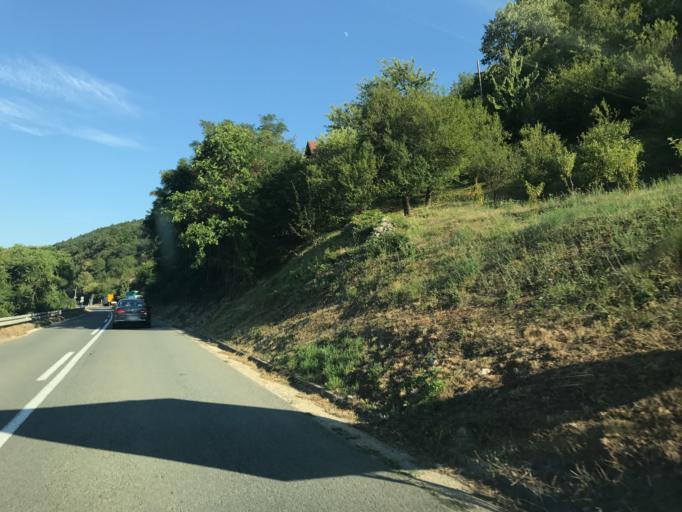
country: RO
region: Mehedinti
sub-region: Comuna Svinita
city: Svinita
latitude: 44.4776
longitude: 22.0976
